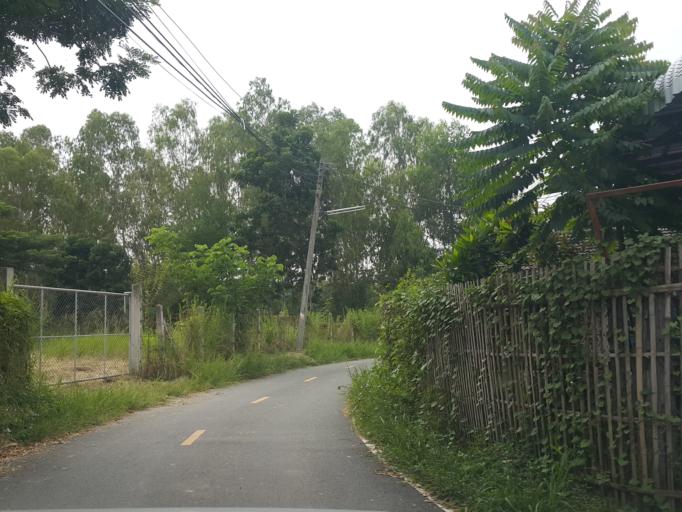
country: TH
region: Chiang Mai
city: San Sai
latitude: 18.8001
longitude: 99.0749
